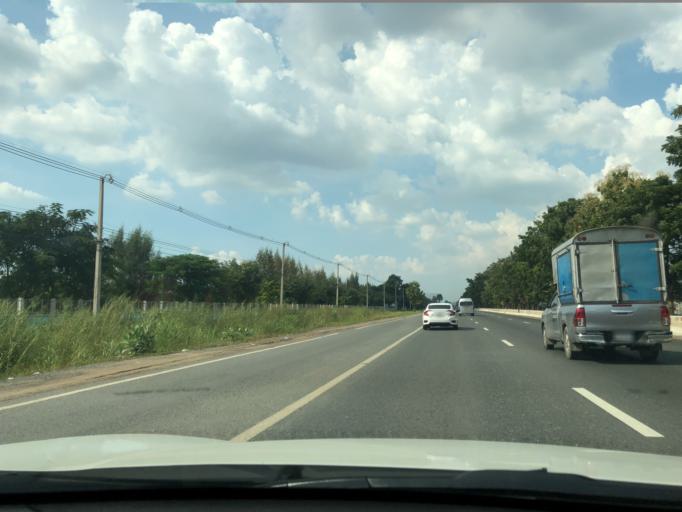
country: TH
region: Nakhon Sawan
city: Krok Phra
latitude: 15.5803
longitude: 100.1245
